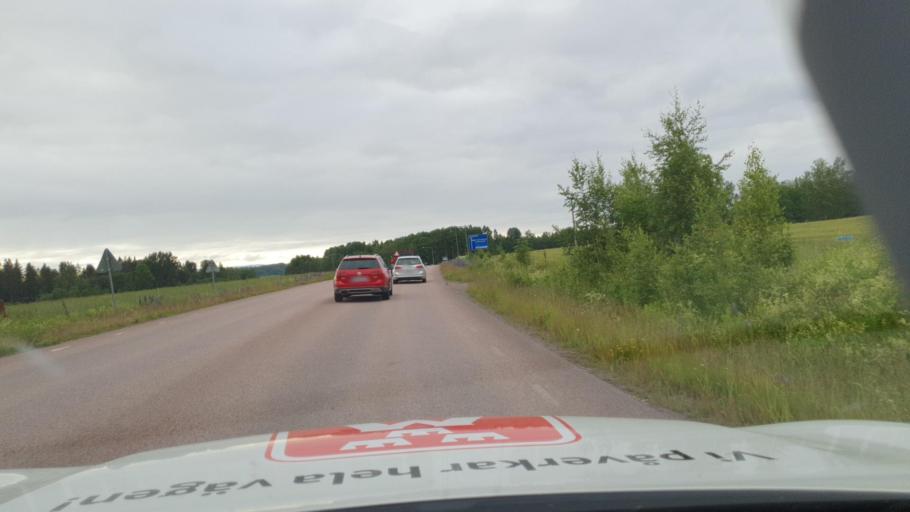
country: SE
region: Vaermland
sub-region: Kils Kommun
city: Kil
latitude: 59.5178
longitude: 13.3066
